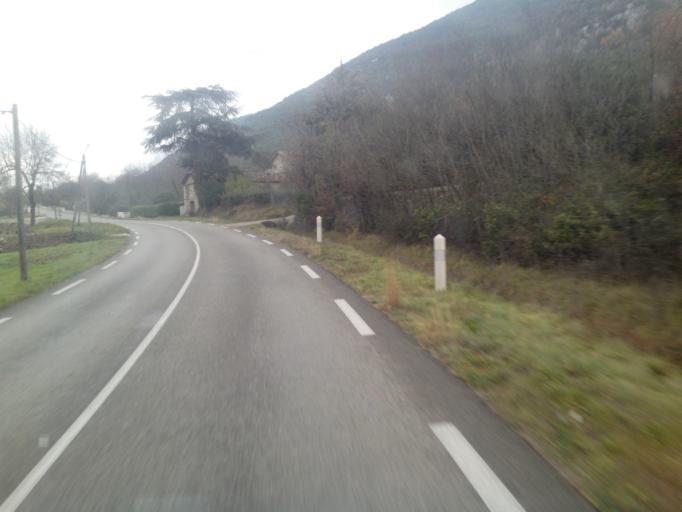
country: FR
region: Languedoc-Roussillon
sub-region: Departement du Gard
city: Saint-Hippolyte-du-Fort
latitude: 43.9589
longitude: 3.8310
